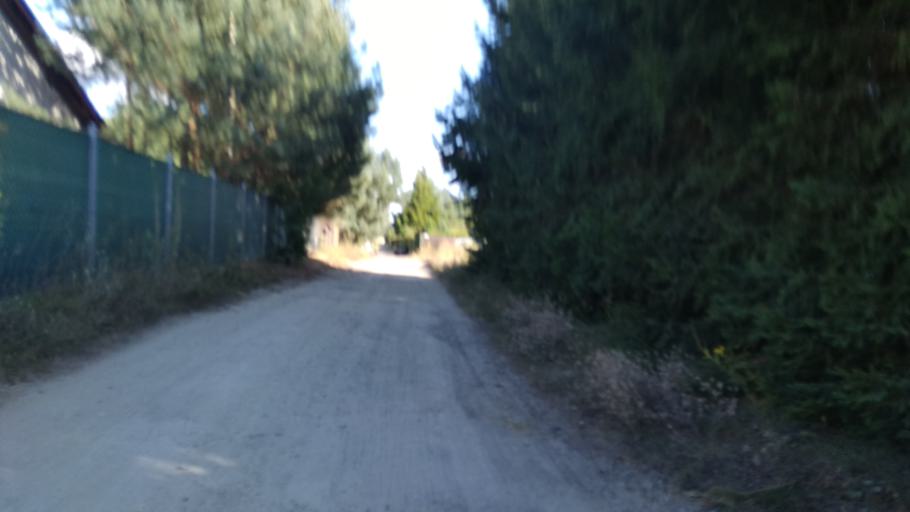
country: PL
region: Kujawsko-Pomorskie
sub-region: Powiat bydgoski
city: Osielsko
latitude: 53.2313
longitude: 18.1202
